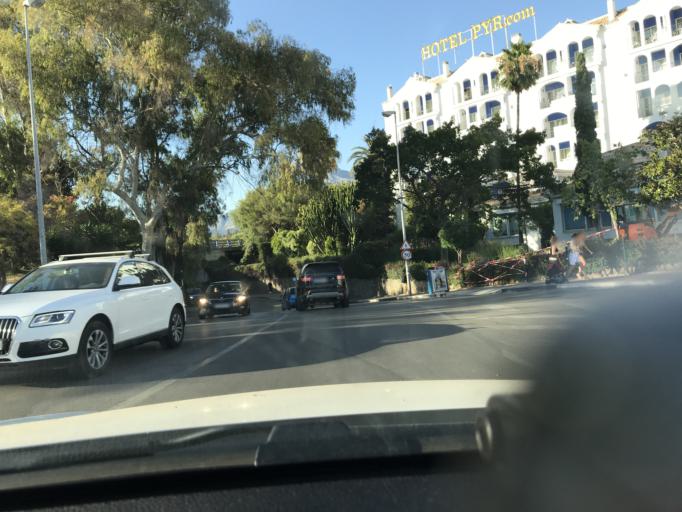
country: ES
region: Andalusia
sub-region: Provincia de Malaga
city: Marbella
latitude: 36.4885
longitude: -4.9564
